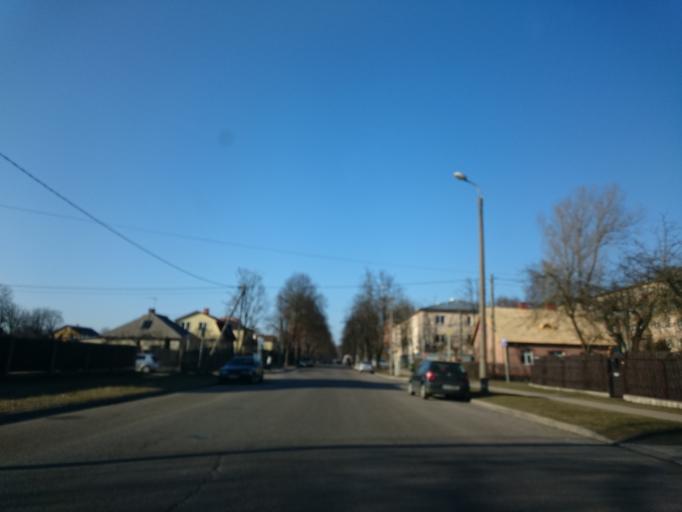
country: LV
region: Riga
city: Bergi
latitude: 56.9843
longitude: 24.2396
